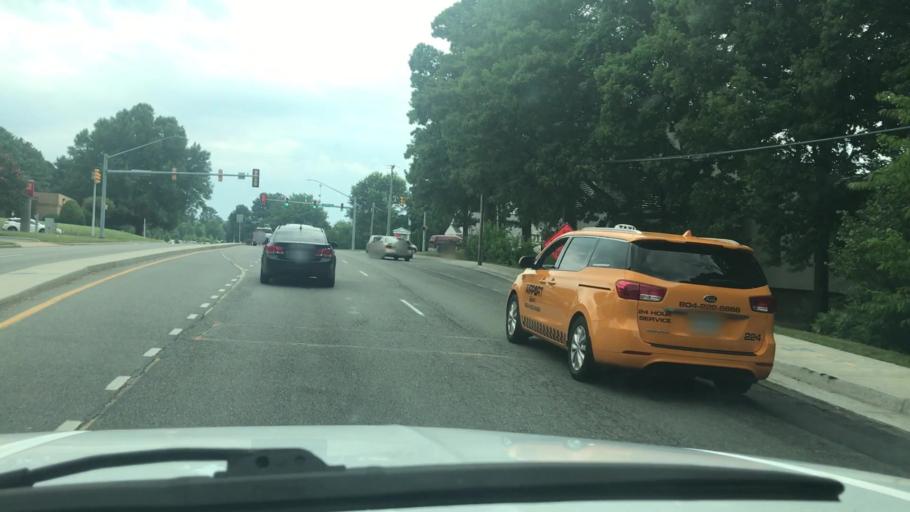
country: US
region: Virginia
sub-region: Henrico County
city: Tuckahoe
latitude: 37.6082
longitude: -77.5645
